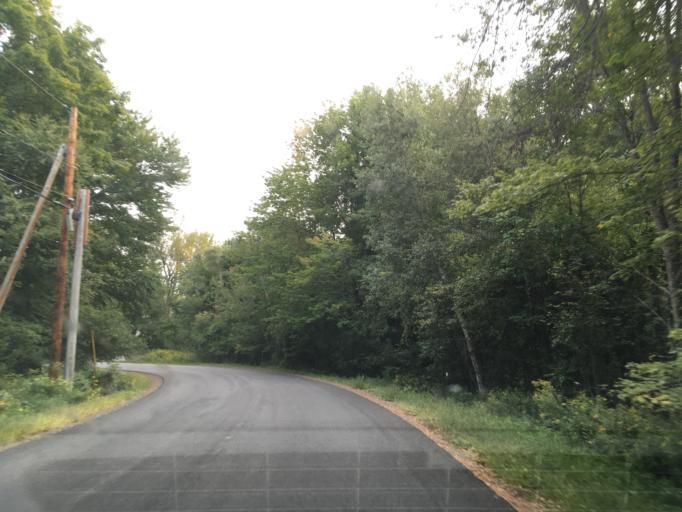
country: US
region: New Hampshire
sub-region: Rockingham County
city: Stratham Station
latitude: 43.0116
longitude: -70.8887
